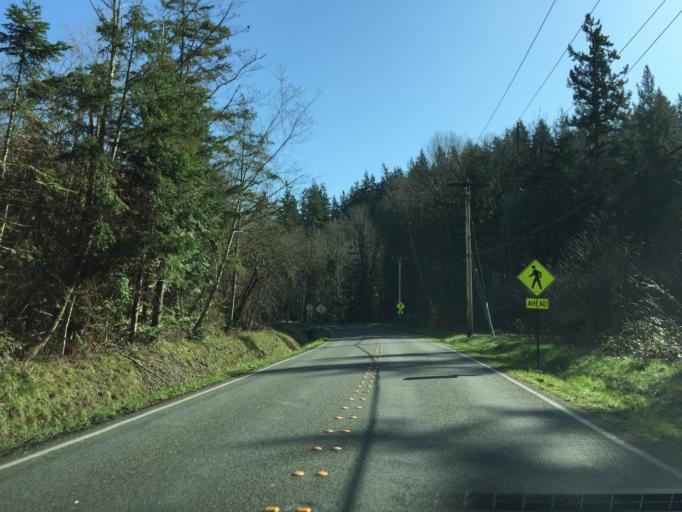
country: US
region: Washington
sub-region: Whatcom County
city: Bellingham
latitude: 48.7026
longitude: -122.4884
